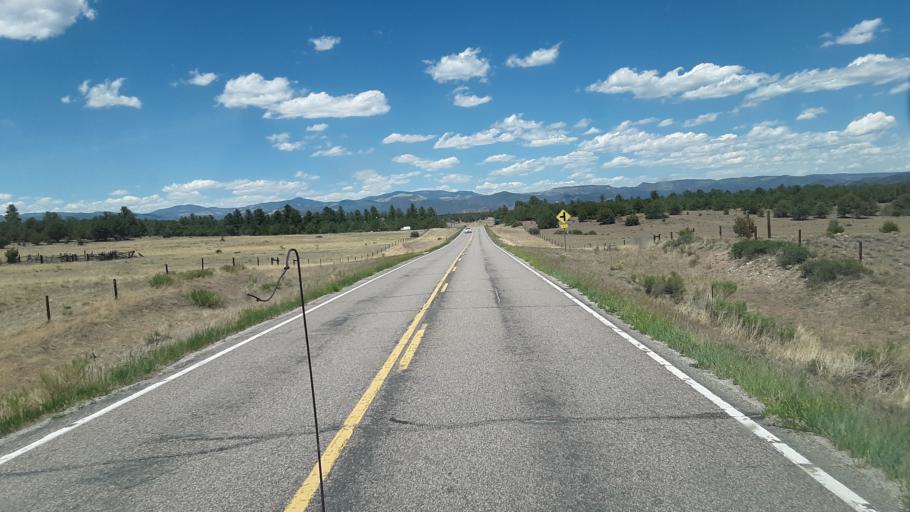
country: US
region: Colorado
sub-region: Custer County
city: Westcliffe
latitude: 38.3058
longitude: -105.6203
